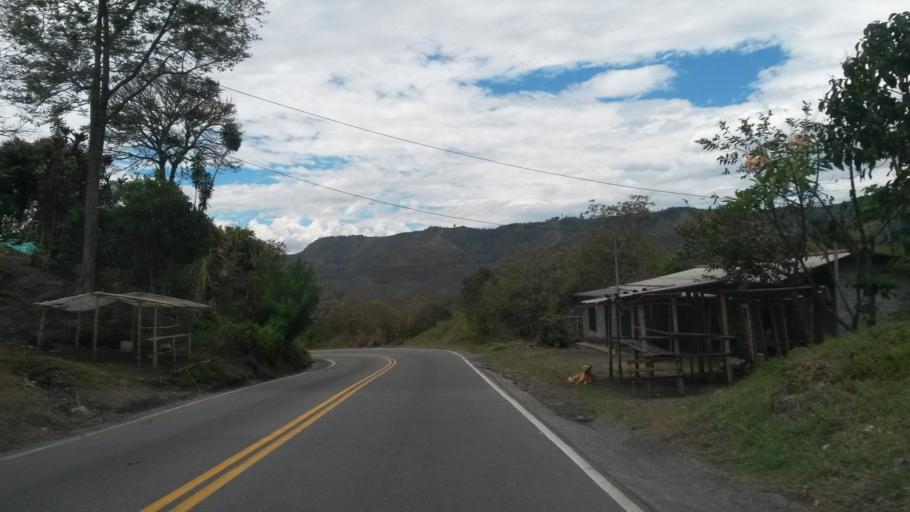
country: CO
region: Cauca
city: Rosas
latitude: 2.2782
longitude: -76.7252
